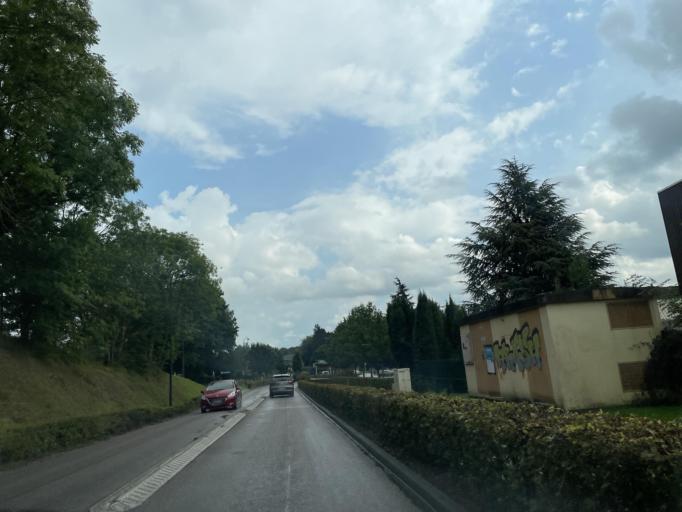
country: FR
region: Haute-Normandie
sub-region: Departement de la Seine-Maritime
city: Envermeu
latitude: 49.8923
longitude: 1.2725
